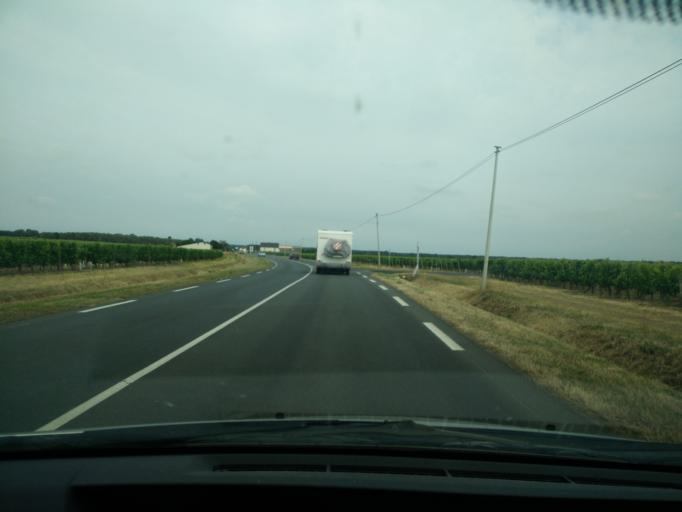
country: FR
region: Pays de la Loire
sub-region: Departement de Maine-et-Loire
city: Montreuil-Bellay
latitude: 47.1418
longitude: -0.1614
